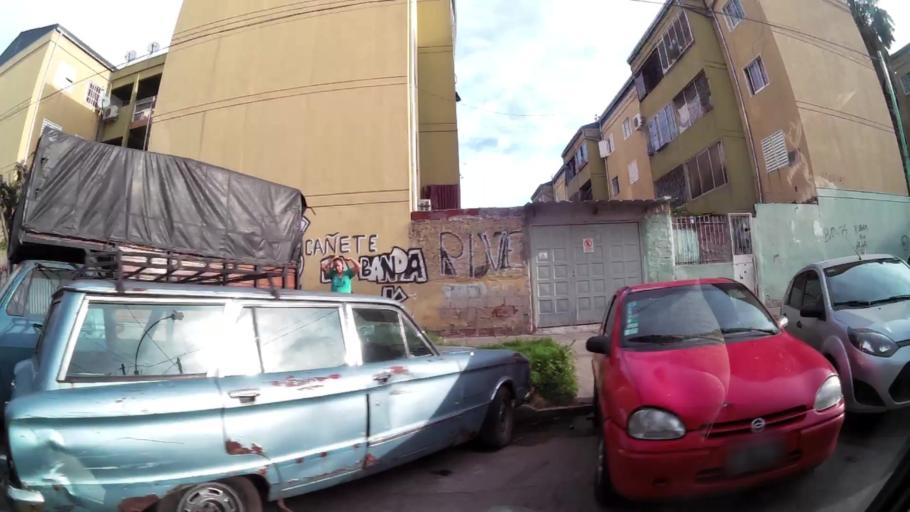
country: AR
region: Buenos Aires F.D.
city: Villa Lugano
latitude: -34.6474
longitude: -58.4397
